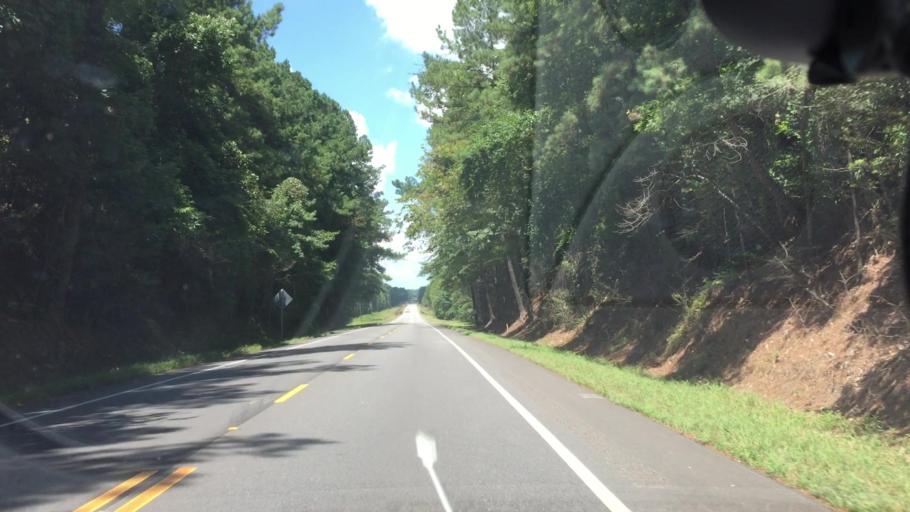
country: US
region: Alabama
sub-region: Coffee County
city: New Brockton
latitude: 31.4660
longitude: -85.9005
